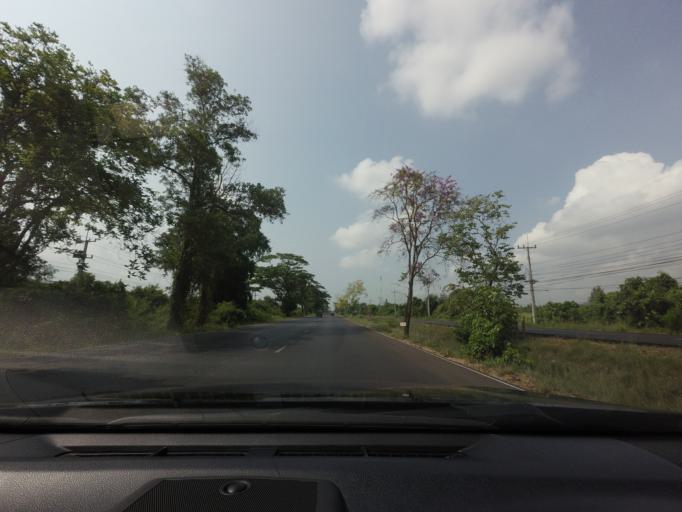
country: TH
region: Prachuap Khiri Khan
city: Sam Roi Yot
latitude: 12.3084
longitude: 99.8767
